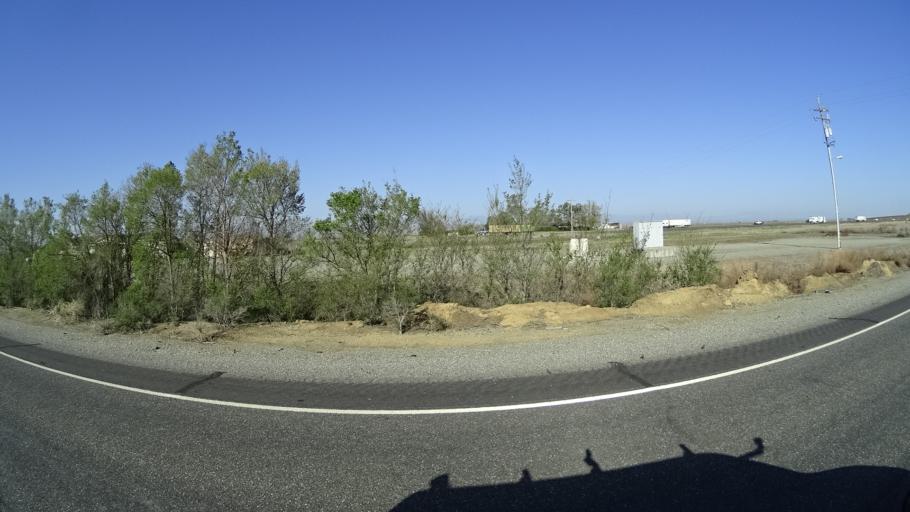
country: US
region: California
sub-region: Glenn County
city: Willows
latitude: 39.4601
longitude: -122.1930
